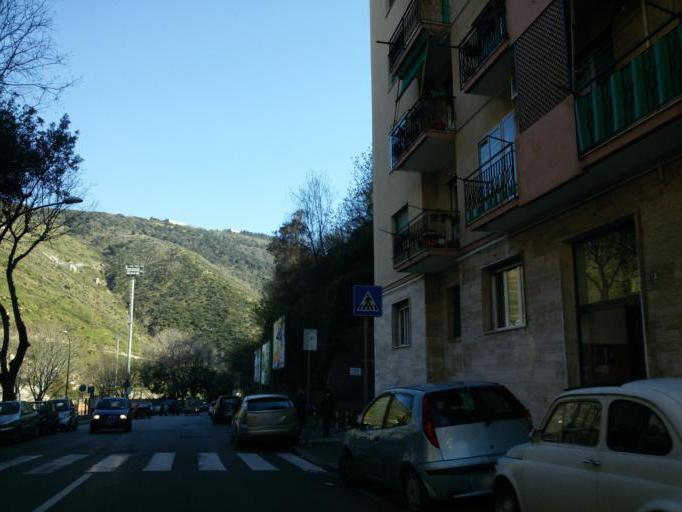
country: IT
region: Liguria
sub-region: Provincia di Genova
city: Genoa
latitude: 44.4252
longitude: 8.9184
